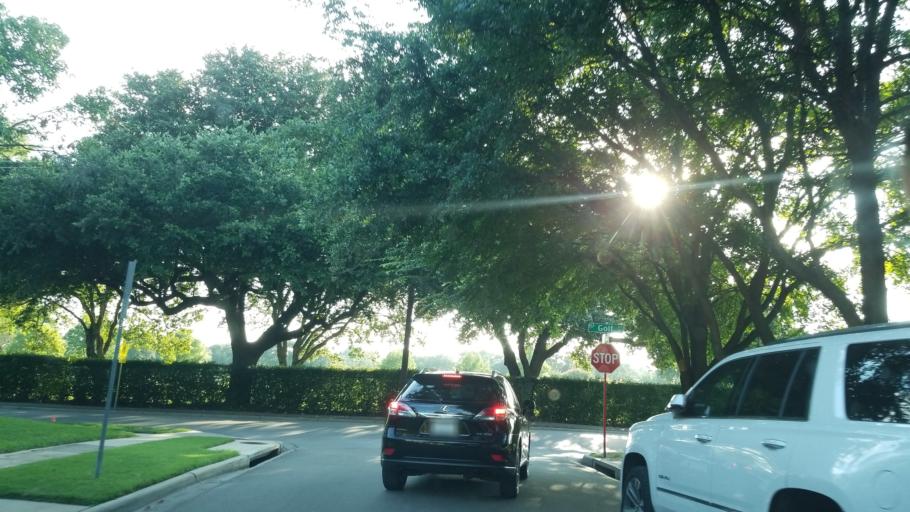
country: US
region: Texas
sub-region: Dallas County
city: University Park
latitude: 32.8428
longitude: -96.7953
